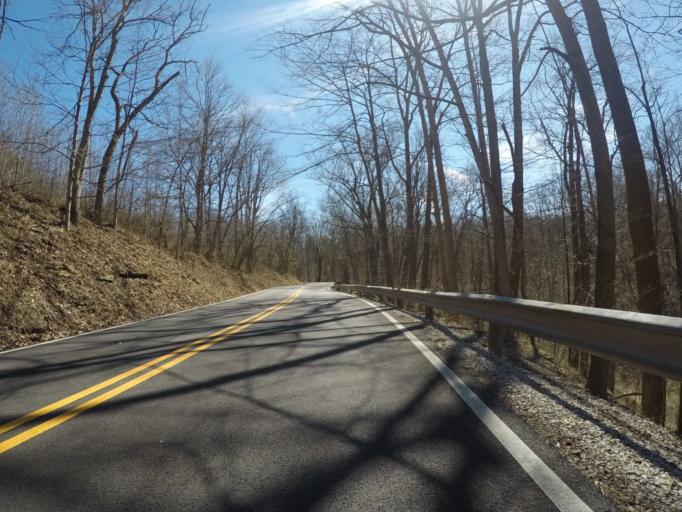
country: US
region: Ohio
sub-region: Lawrence County
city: South Point
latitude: 38.4596
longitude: -82.5542
